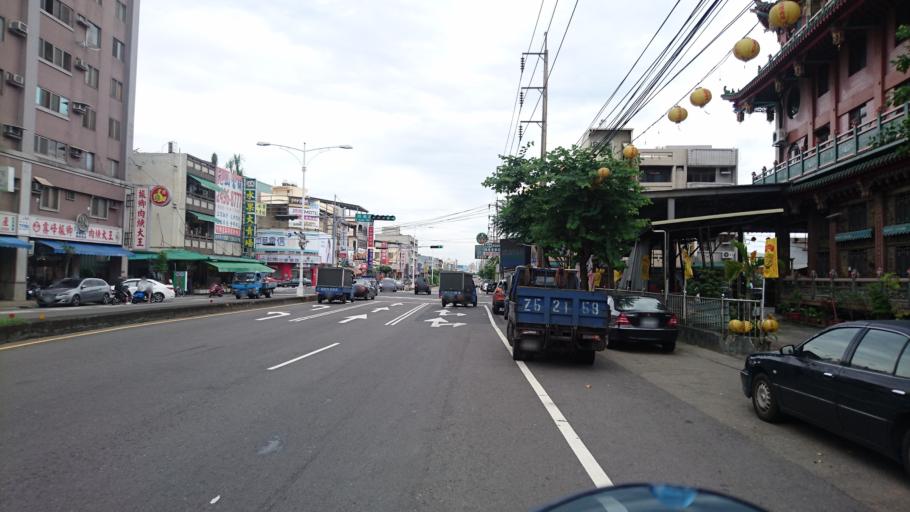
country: TW
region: Taiwan
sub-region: Taichung City
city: Taichung
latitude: 24.0663
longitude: 120.6960
